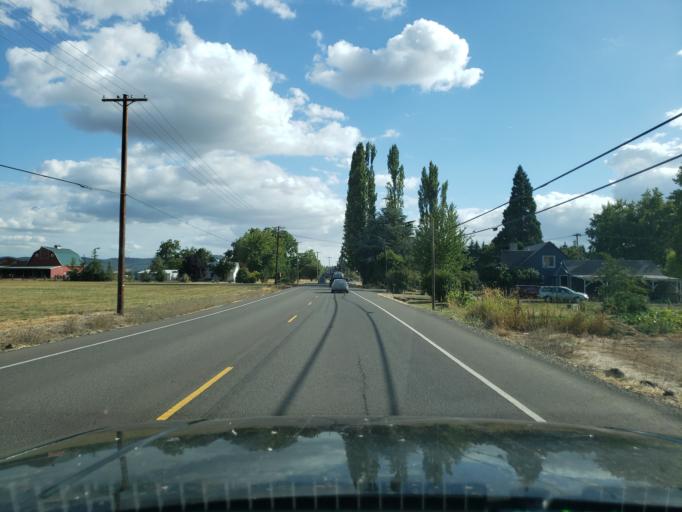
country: US
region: Oregon
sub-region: Yamhill County
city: McMinnville
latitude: 45.1809
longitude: -123.2100
